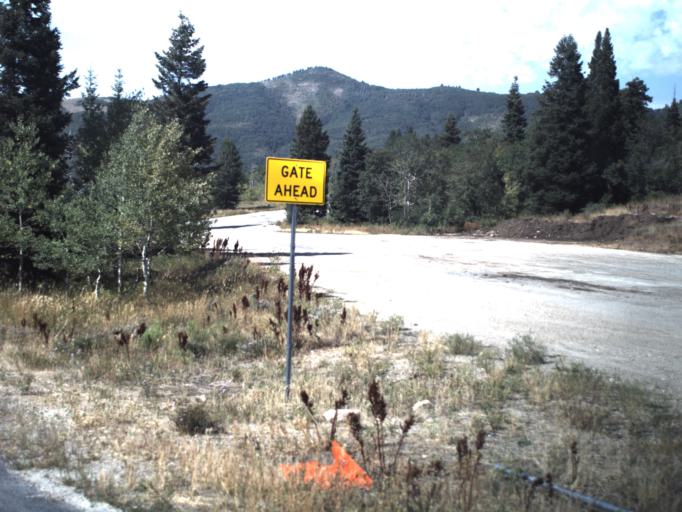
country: US
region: Utah
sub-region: Morgan County
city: Mountain Green
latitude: 41.2209
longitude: -111.8551
